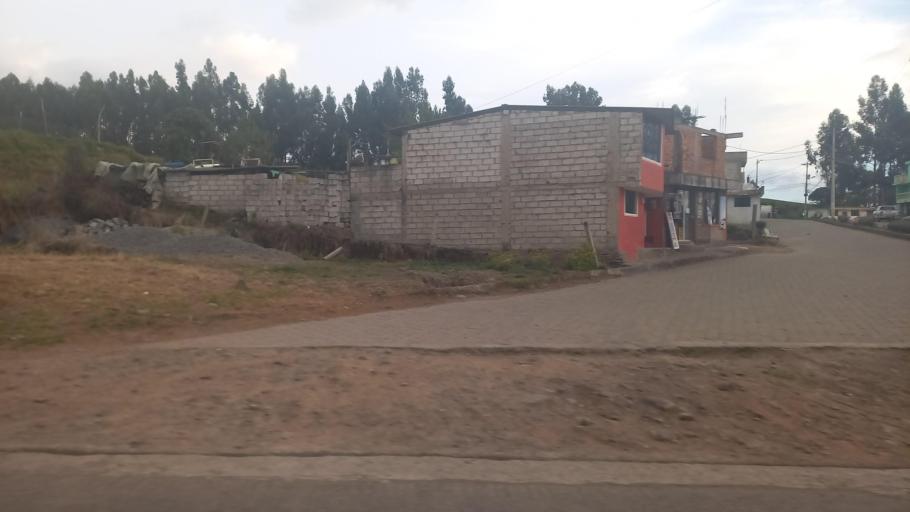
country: EC
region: Pichincha
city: Cayambe
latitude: 0.0913
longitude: -78.0991
